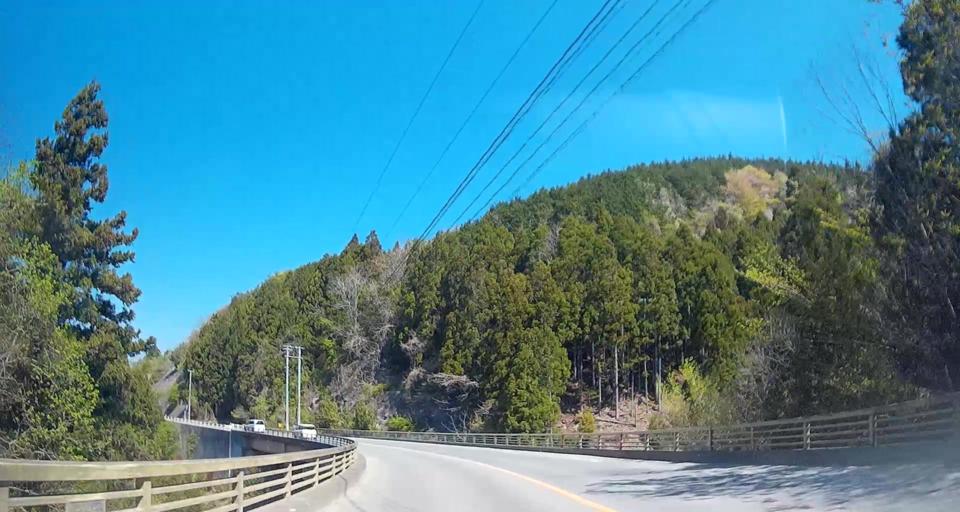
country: JP
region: Miyagi
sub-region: Oshika Gun
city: Onagawa Cho
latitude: 38.5312
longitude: 141.4384
